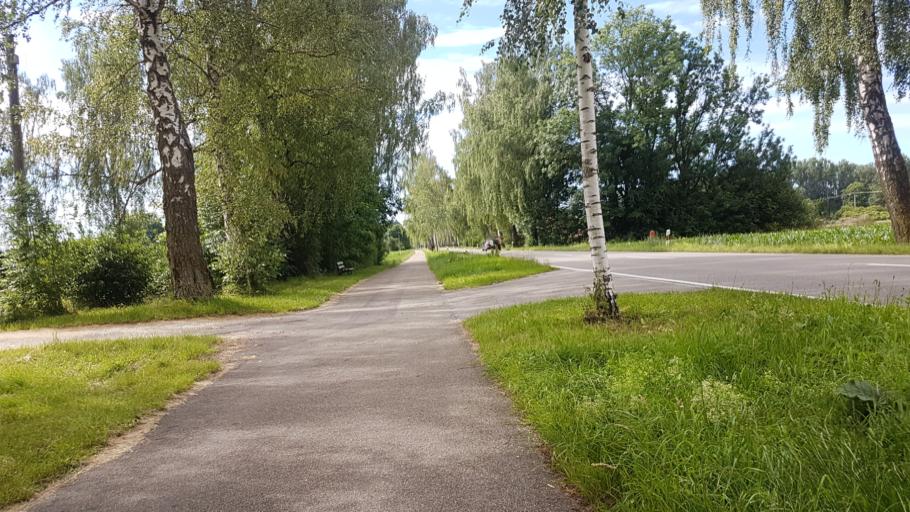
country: DE
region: Bavaria
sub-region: Swabia
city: Guenzburg
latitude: 48.4738
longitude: 10.2627
